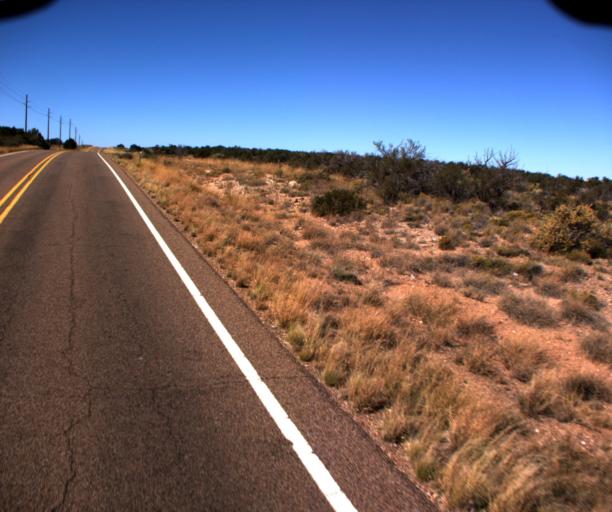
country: US
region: Arizona
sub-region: Navajo County
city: Taylor
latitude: 34.5105
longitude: -110.1705
